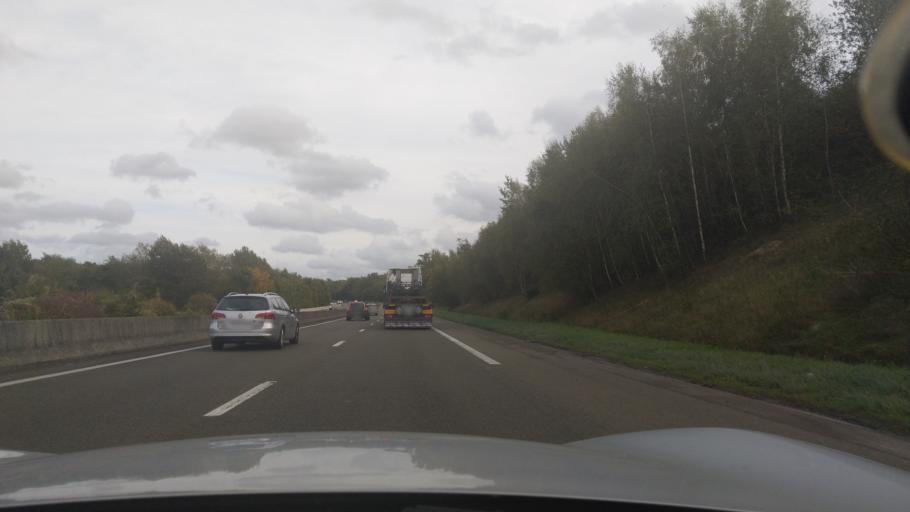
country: FR
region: Ile-de-France
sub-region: Departement du Val-d'Oise
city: Meriel
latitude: 49.0711
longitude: 2.2455
